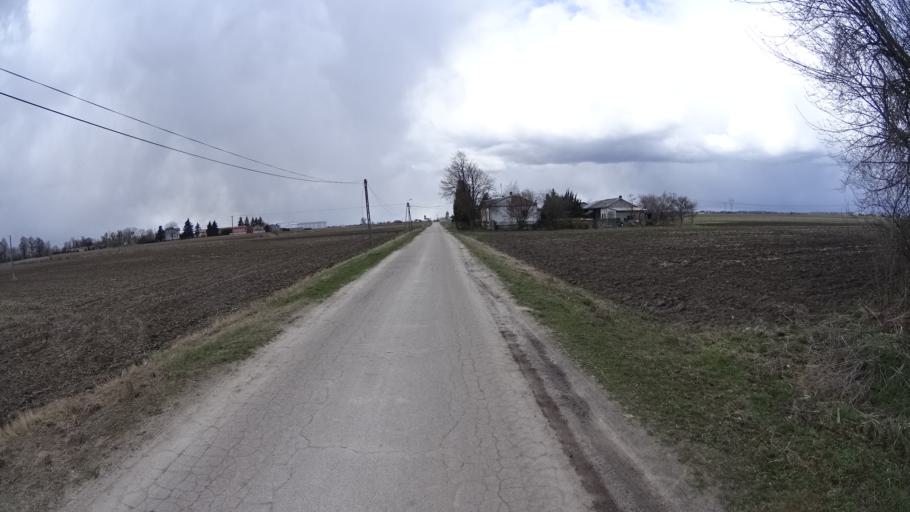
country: PL
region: Masovian Voivodeship
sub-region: Powiat warszawski zachodni
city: Jozefow
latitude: 52.2217
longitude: 20.6820
